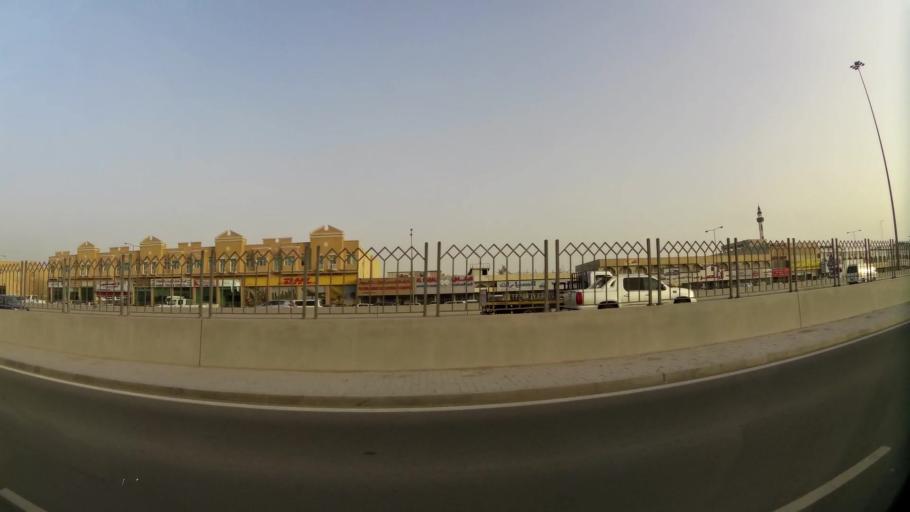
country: QA
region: Baladiyat ar Rayyan
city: Ar Rayyan
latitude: 25.2380
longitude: 51.4526
